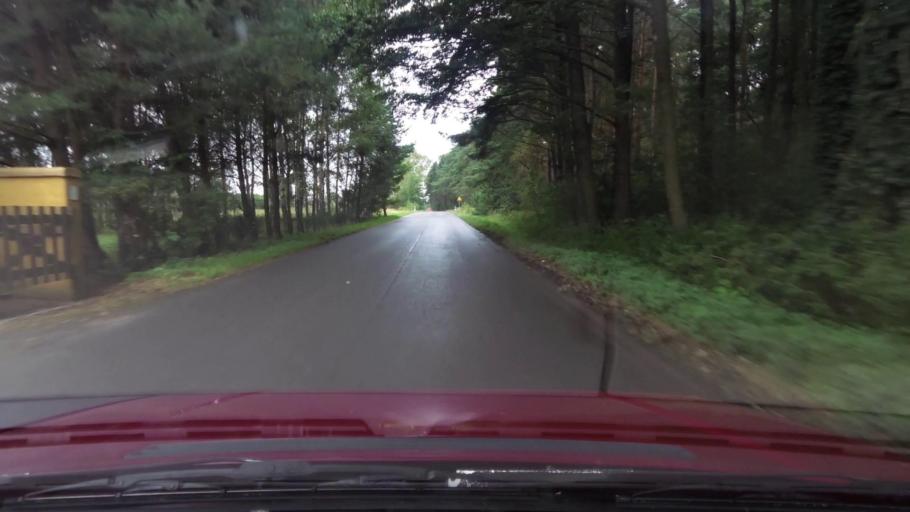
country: PL
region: West Pomeranian Voivodeship
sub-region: Powiat kolobrzeski
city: Grzybowo
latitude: 54.1525
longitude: 15.5039
